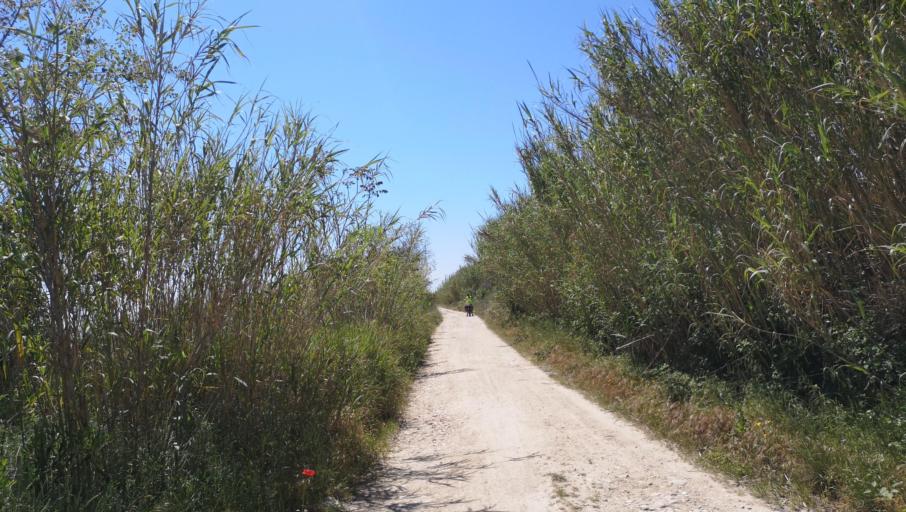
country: IT
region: The Marches
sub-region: Province of Fermo
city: Campofilone
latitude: 43.0611
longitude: 13.8498
